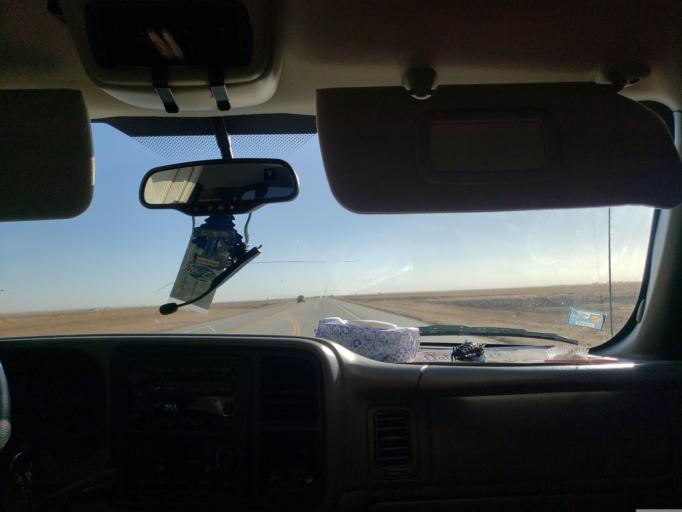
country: US
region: Kansas
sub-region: Finney County
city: Garden City
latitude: 37.7681
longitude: -100.8716
